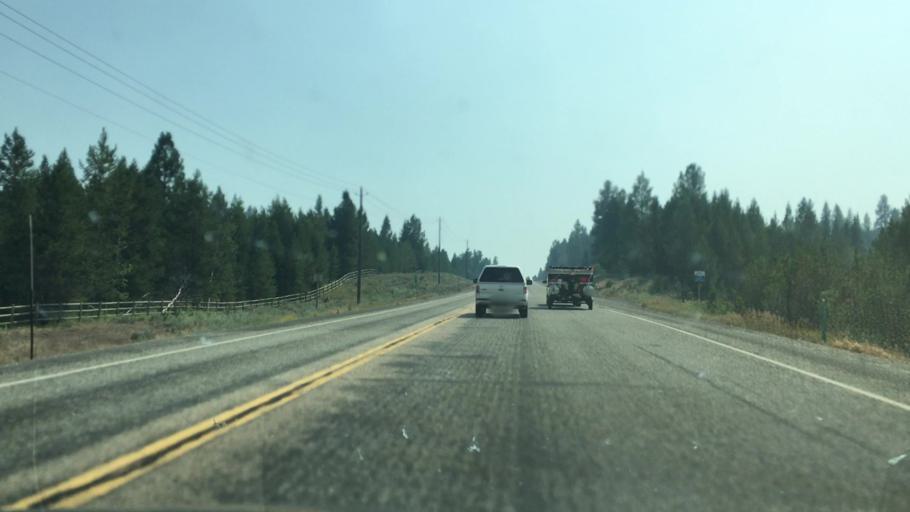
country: US
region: Idaho
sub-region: Valley County
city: Cascade
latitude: 44.3822
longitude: -116.0131
